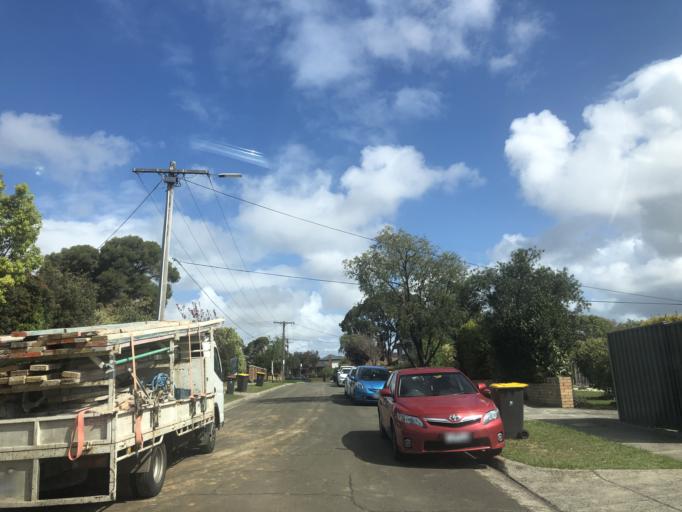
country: AU
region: Victoria
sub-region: Monash
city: Ashwood
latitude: -37.8752
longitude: 145.1150
